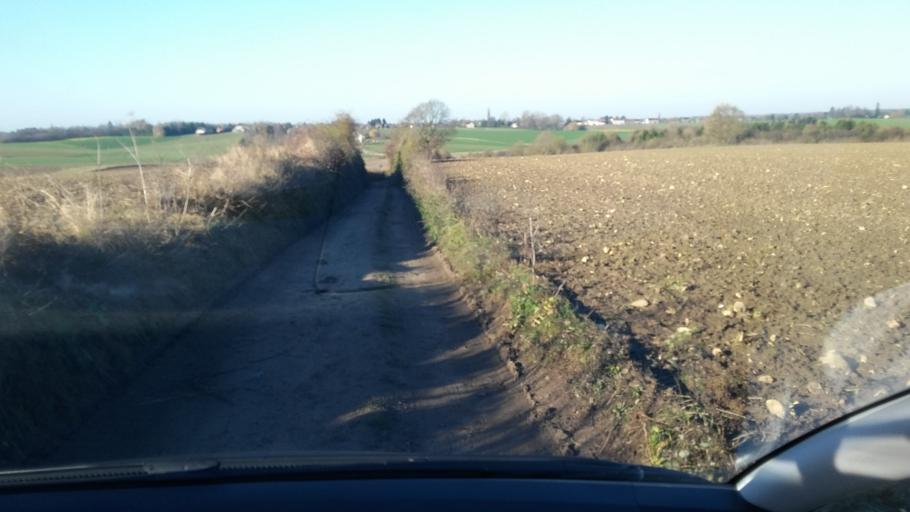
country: BE
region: Wallonia
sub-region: Province du Brabant Wallon
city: Waterloo
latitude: 50.6852
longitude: 4.4304
